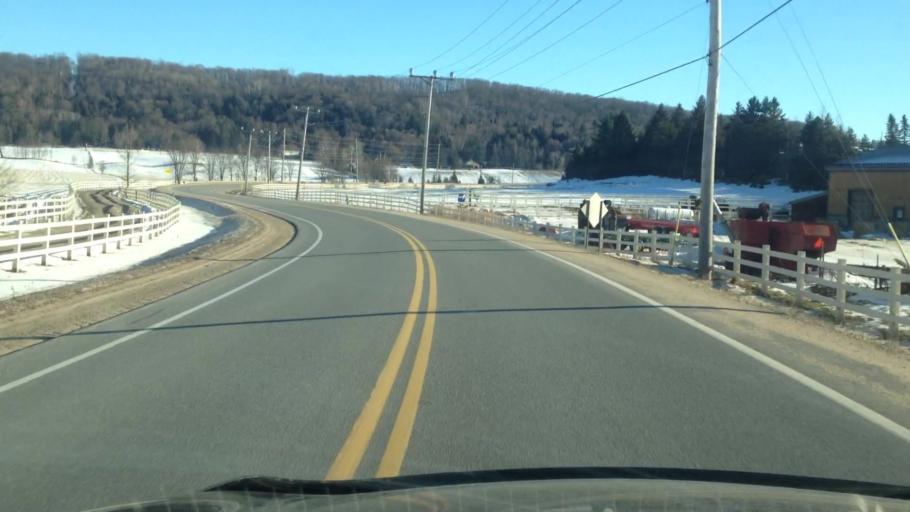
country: CA
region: Quebec
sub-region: Laurentides
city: Mont-Tremblant
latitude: 46.0404
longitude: -74.6051
